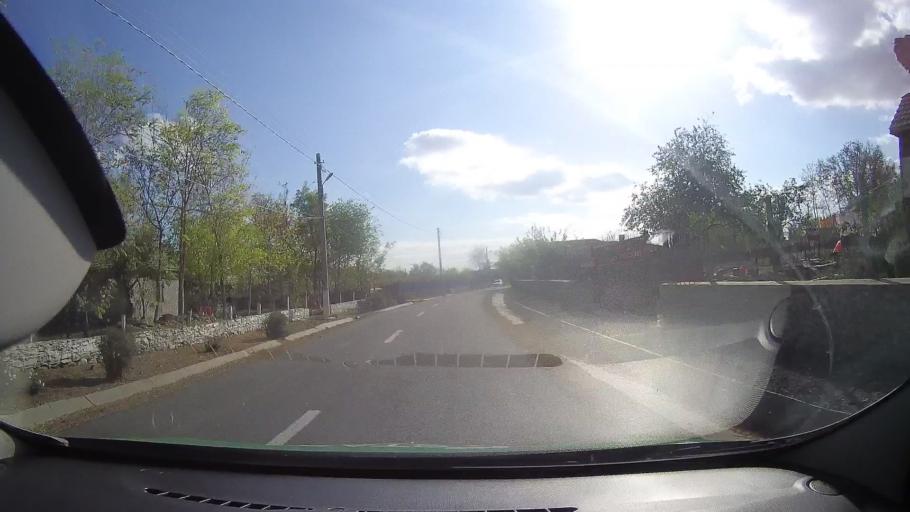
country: RO
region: Constanta
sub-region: Comuna Istria
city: Istria
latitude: 44.5748
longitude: 28.7137
